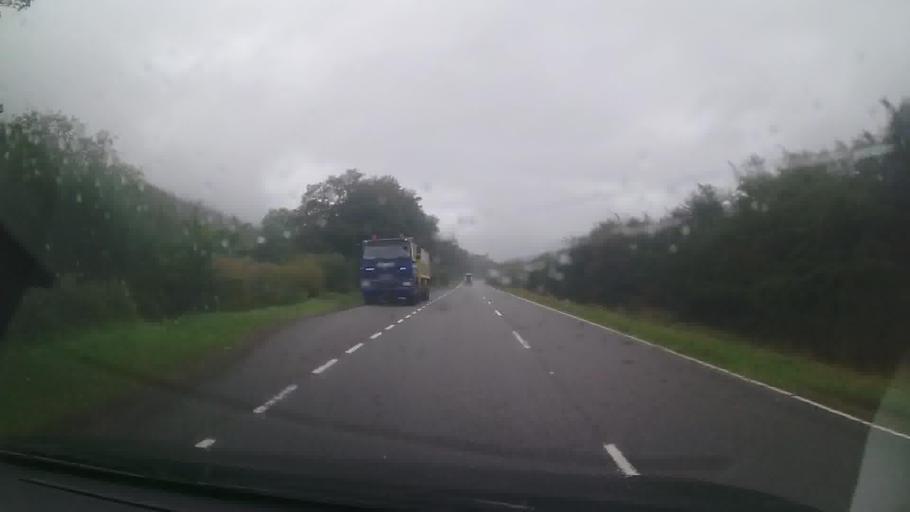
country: GB
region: Scotland
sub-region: Highland
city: Fort William
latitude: 56.6677
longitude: -5.0769
